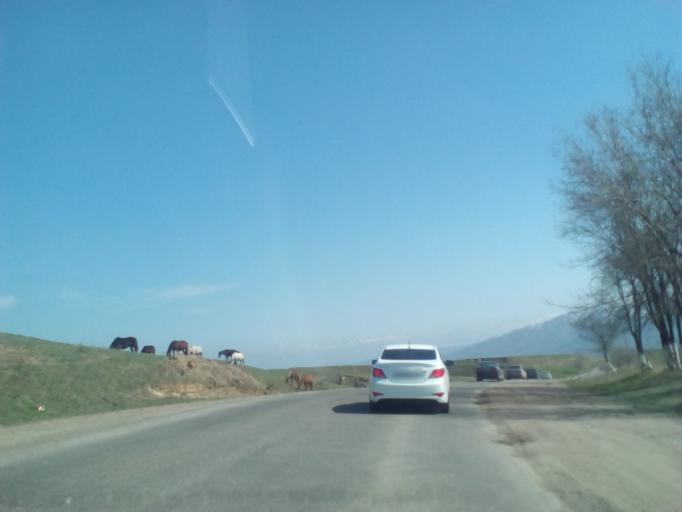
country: KZ
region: Almaty Oblysy
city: Burunday
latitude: 43.1792
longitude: 76.4246
